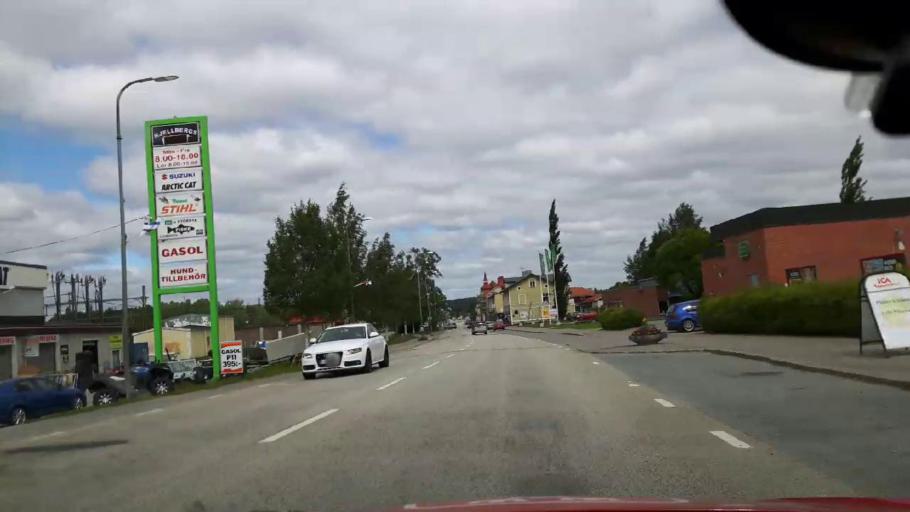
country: SE
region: Jaemtland
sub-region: Braecke Kommun
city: Braecke
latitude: 62.7495
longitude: 15.4189
